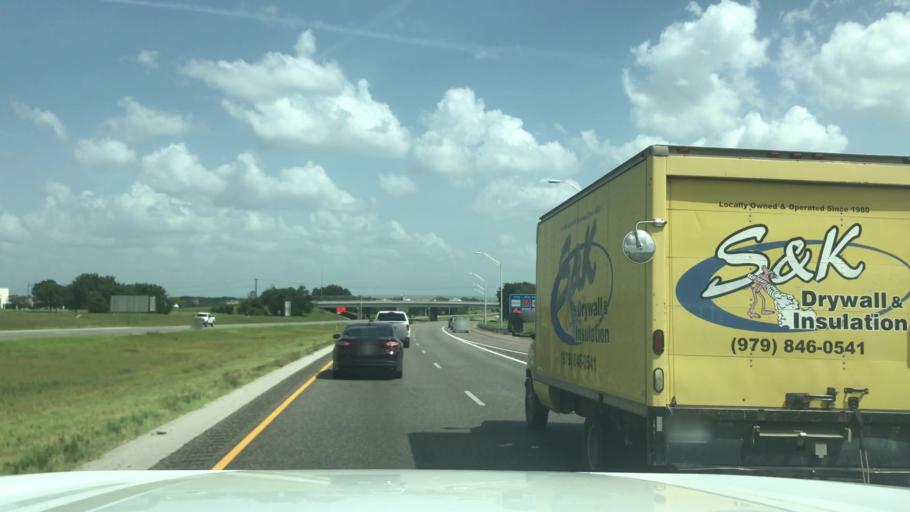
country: US
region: Texas
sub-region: Brazos County
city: College Station
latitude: 30.6656
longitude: -96.3303
